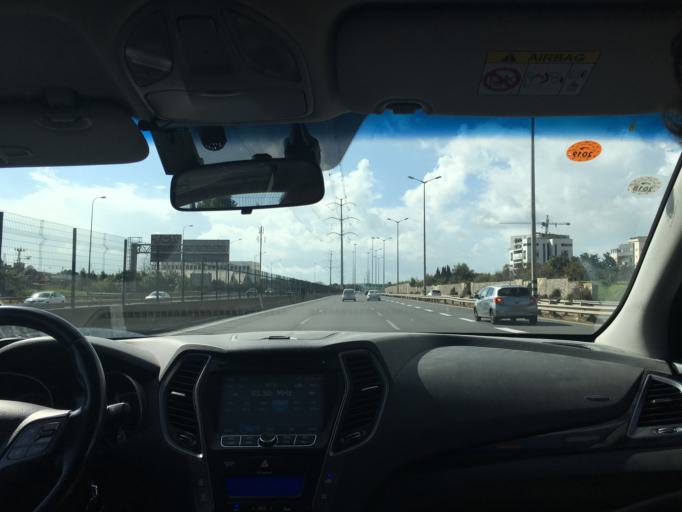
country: IL
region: Tel Aviv
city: Bene Beraq
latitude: 32.0627
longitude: 34.8370
